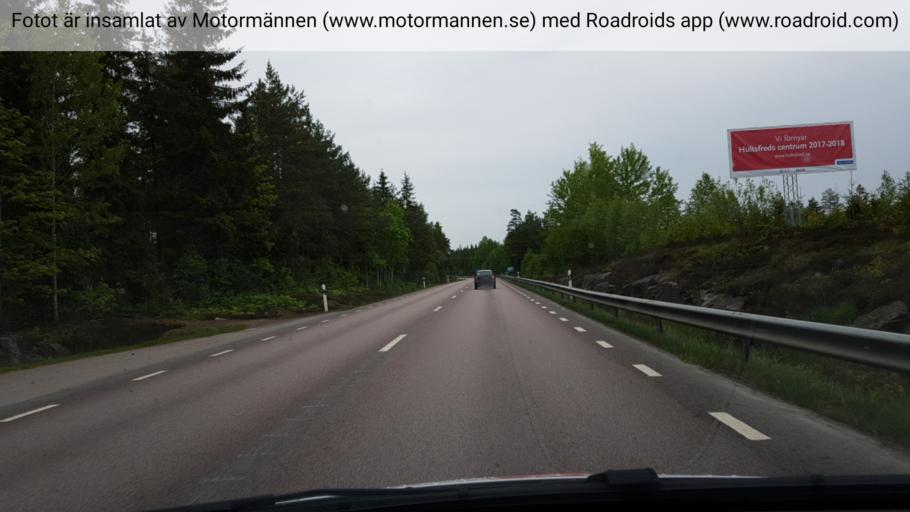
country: SE
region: Kalmar
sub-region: Hultsfreds Kommun
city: Hultsfred
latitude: 57.4632
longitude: 15.8393
